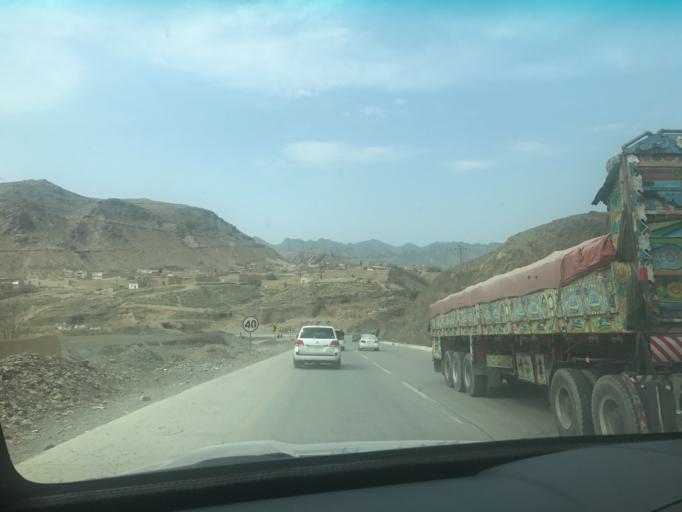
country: PK
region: Federally Administered Tribal Areas
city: Landi Kotal
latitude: 34.1009
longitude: 71.1390
